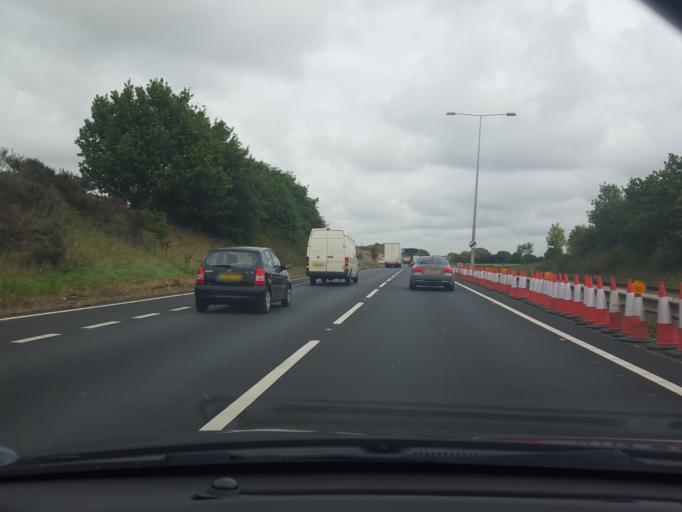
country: GB
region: England
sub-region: Suffolk
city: Capel Saint Mary
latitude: 52.0189
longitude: 1.0772
